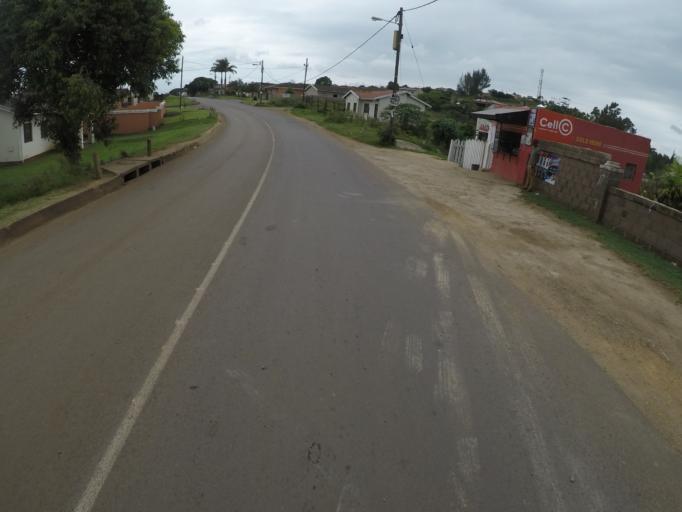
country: ZA
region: KwaZulu-Natal
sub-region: uThungulu District Municipality
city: Empangeni
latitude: -28.7854
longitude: 31.8527
